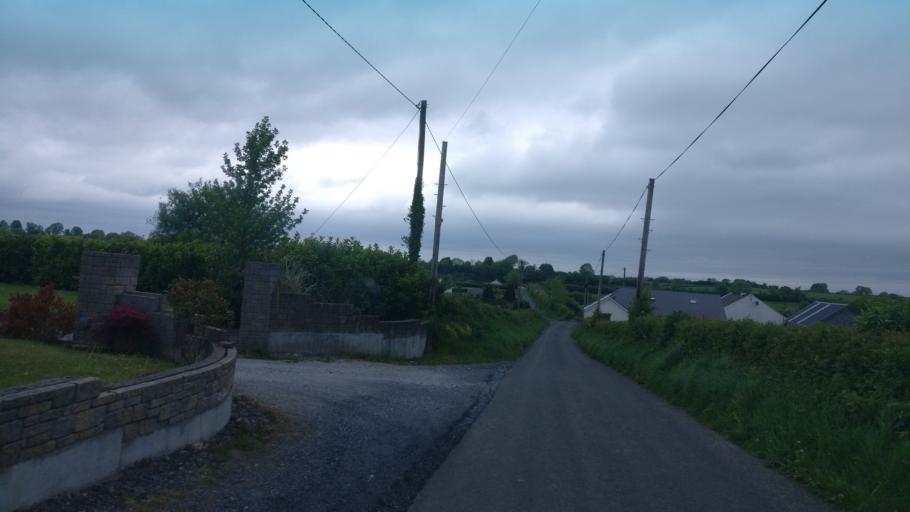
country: IE
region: Connaught
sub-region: County Galway
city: Portumna
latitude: 53.1368
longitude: -8.2913
